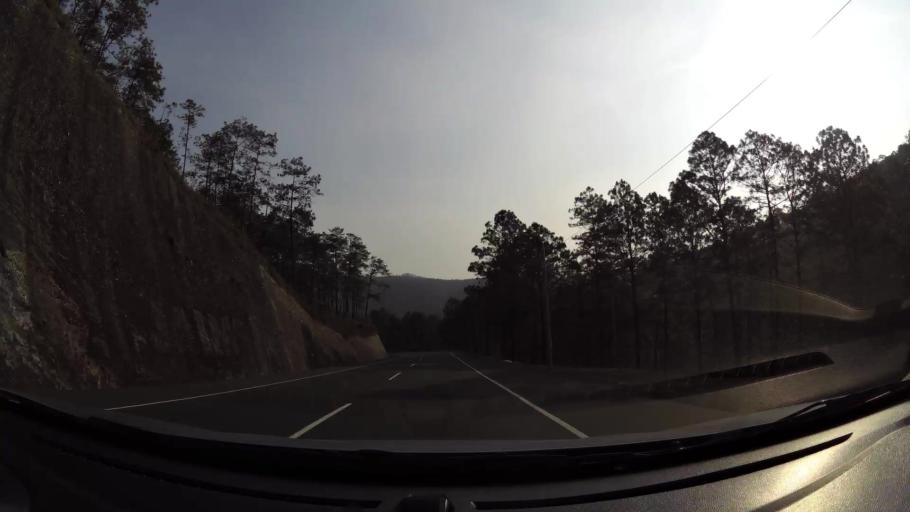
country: HN
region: Francisco Morazan
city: Zambrano
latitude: 14.2829
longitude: -87.4681
